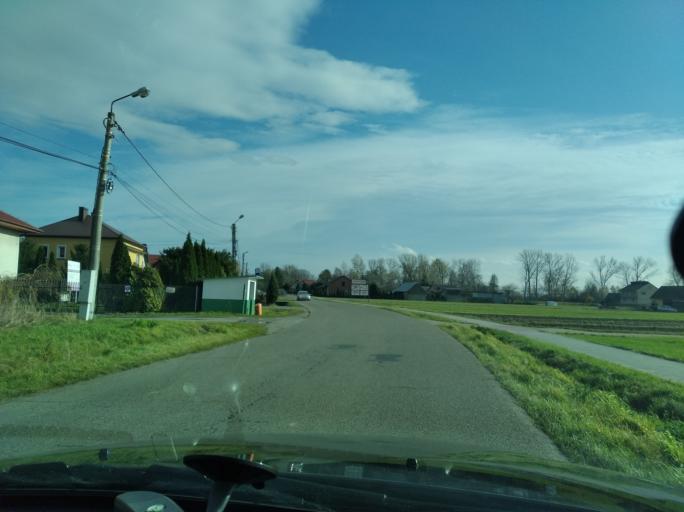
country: PL
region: Subcarpathian Voivodeship
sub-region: Powiat ropczycko-sedziszowski
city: Ostrow
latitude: 50.0959
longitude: 21.6390
